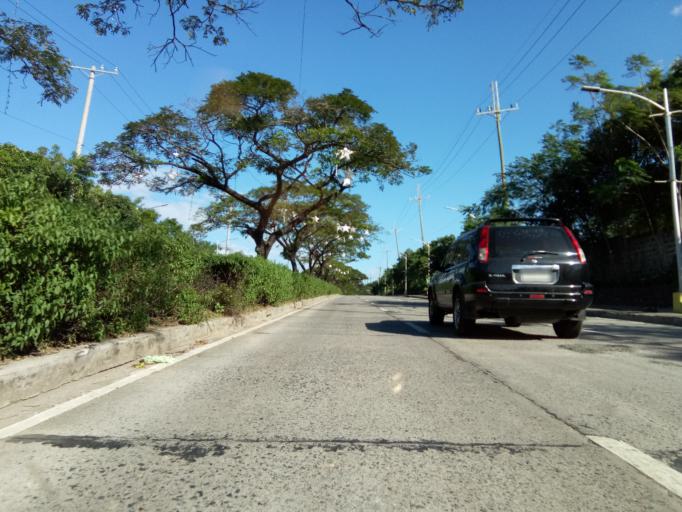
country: PH
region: Calabarzon
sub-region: Province of Cavite
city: Dasmarinas
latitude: 14.3501
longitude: 120.9659
